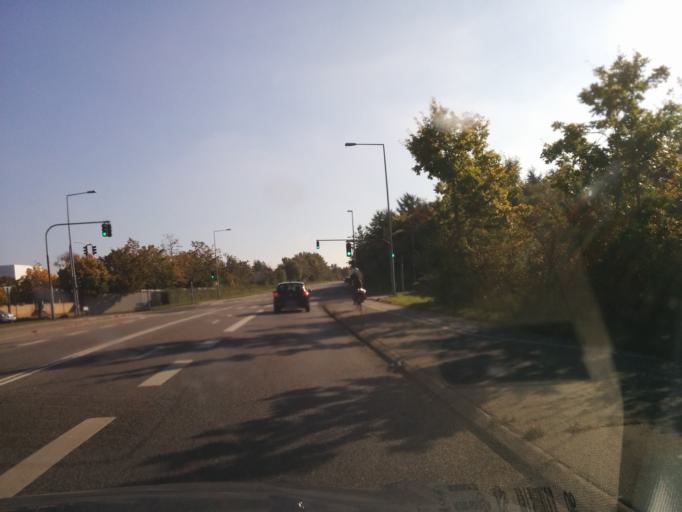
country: DK
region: Central Jutland
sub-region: Arhus Kommune
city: Stavtrup
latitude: 56.1230
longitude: 10.1443
